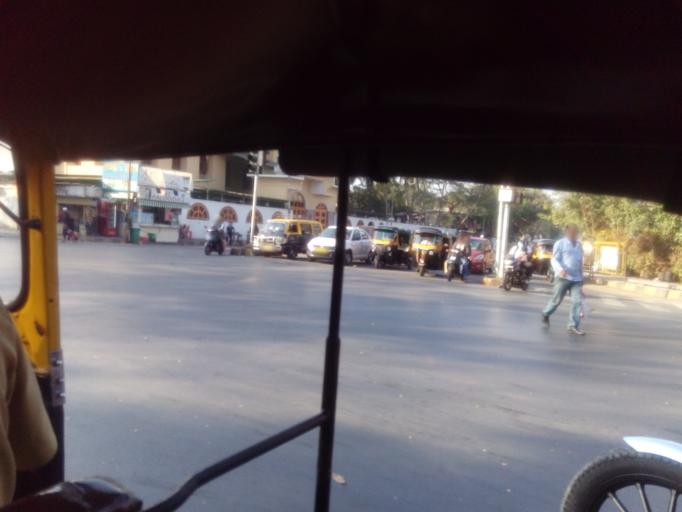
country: IN
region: Maharashtra
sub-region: Mumbai Suburban
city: Mumbai
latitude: 19.0845
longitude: 72.8346
